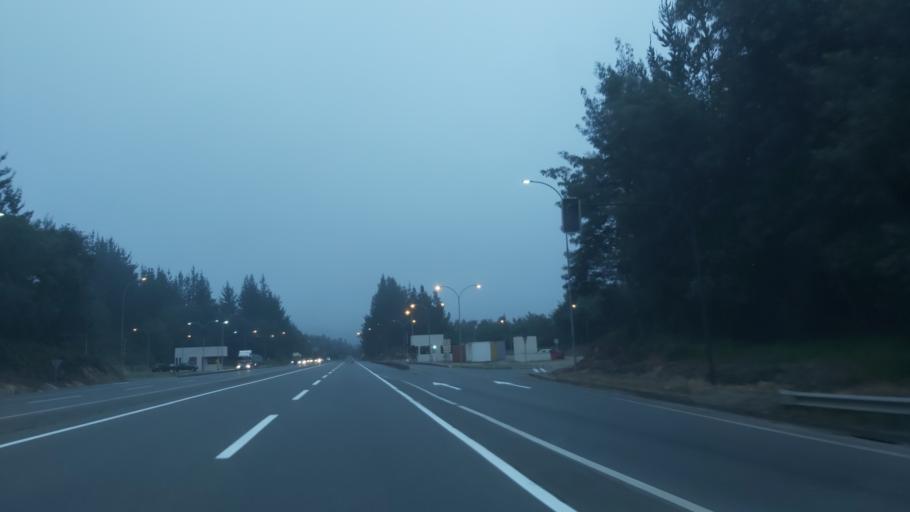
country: CL
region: Biobio
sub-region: Provincia de Concepcion
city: Penco
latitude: -36.7350
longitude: -72.8872
